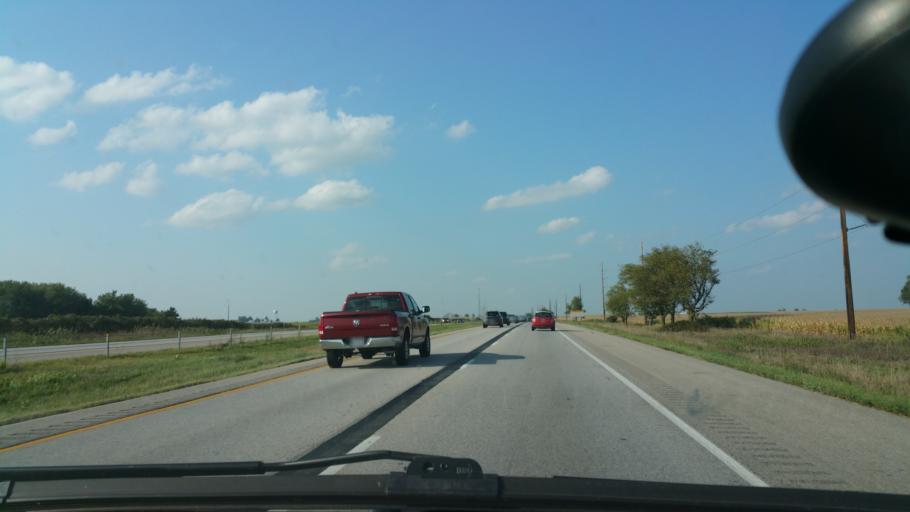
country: US
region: Iowa
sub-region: Polk County
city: Ankeny
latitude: 41.8031
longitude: -93.5701
